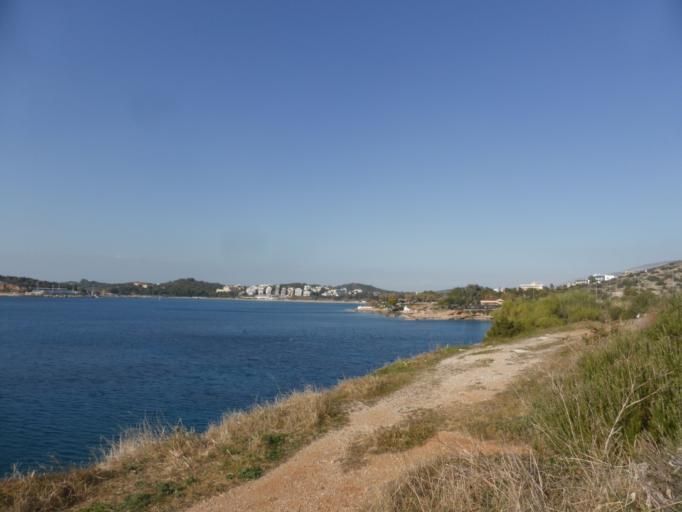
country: GR
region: Attica
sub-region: Nomarchia Anatolikis Attikis
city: Vouliagmeni
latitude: 37.8046
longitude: 23.7846
